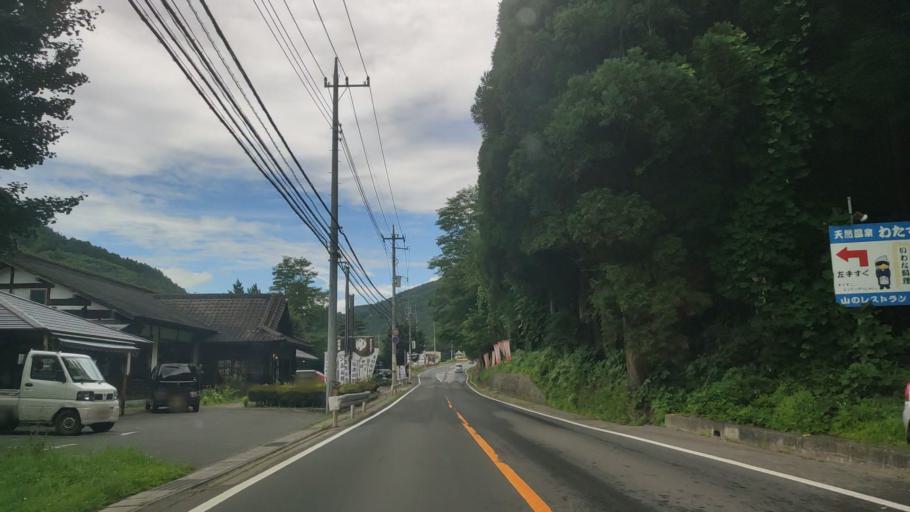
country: JP
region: Gunma
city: Numata
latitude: 36.7396
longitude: 139.2317
